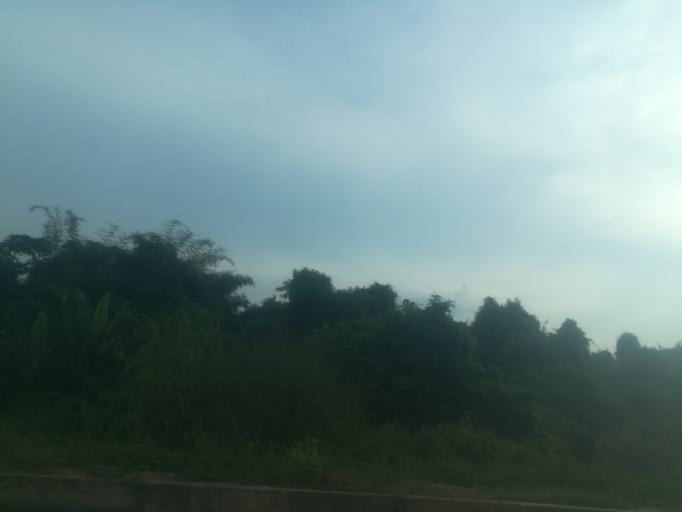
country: NG
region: Ogun
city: Abeokuta
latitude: 7.1618
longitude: 3.3184
